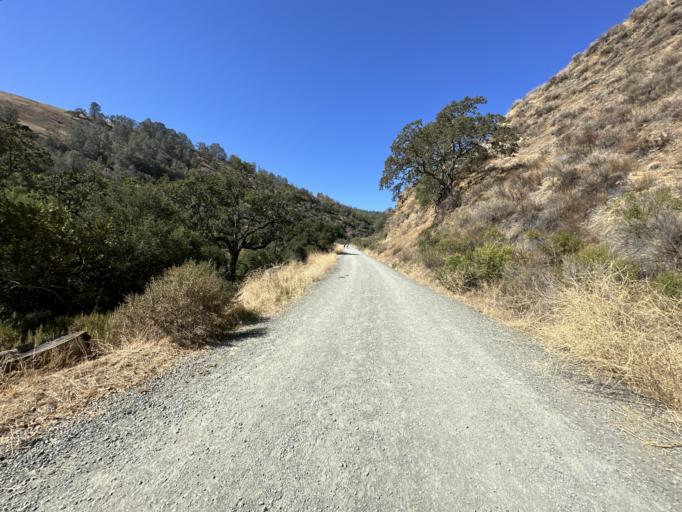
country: US
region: California
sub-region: Santa Clara County
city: Milpitas
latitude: 37.5048
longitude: -121.8251
